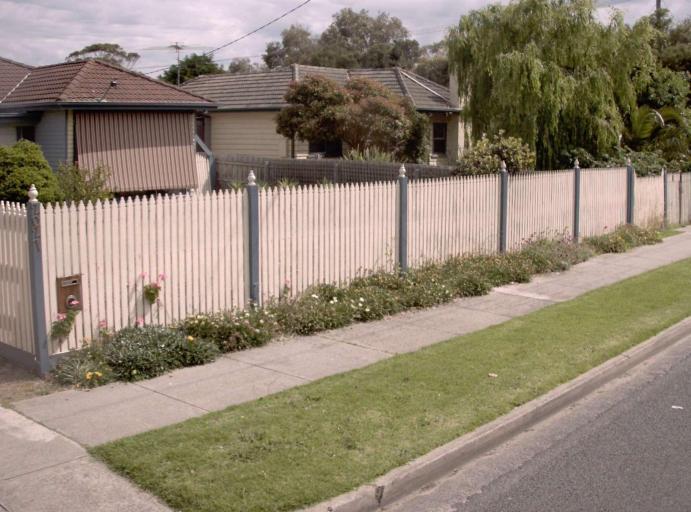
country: AU
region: Victoria
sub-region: Mornington Peninsula
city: Tootgarook
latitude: -38.3705
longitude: 144.8430
